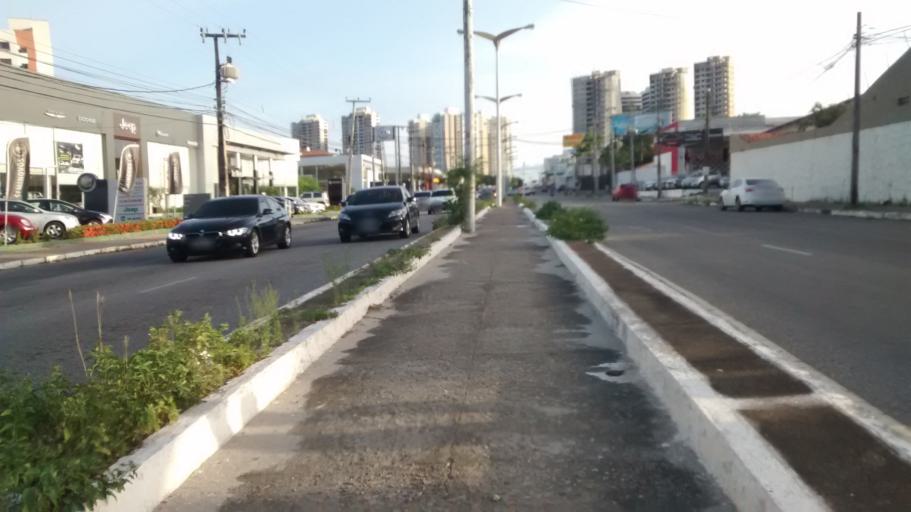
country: BR
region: Ceara
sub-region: Fortaleza
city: Fortaleza
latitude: -3.7602
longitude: -38.4925
